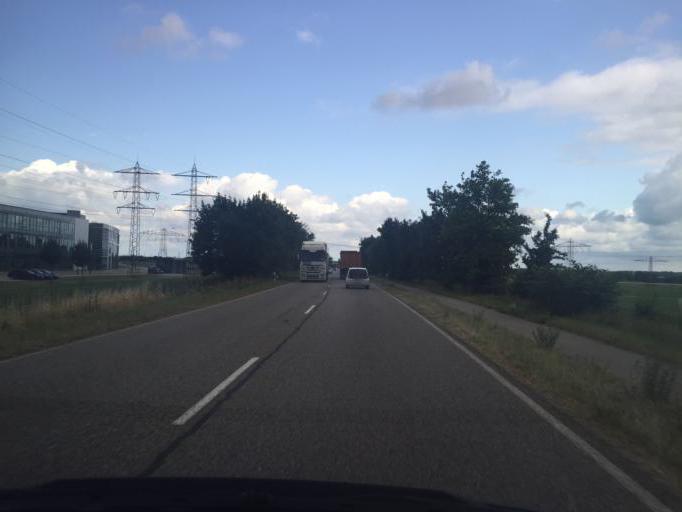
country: DE
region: Baden-Wuerttemberg
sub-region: Karlsruhe Region
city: Bruchsal
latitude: 49.1280
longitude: 8.5771
